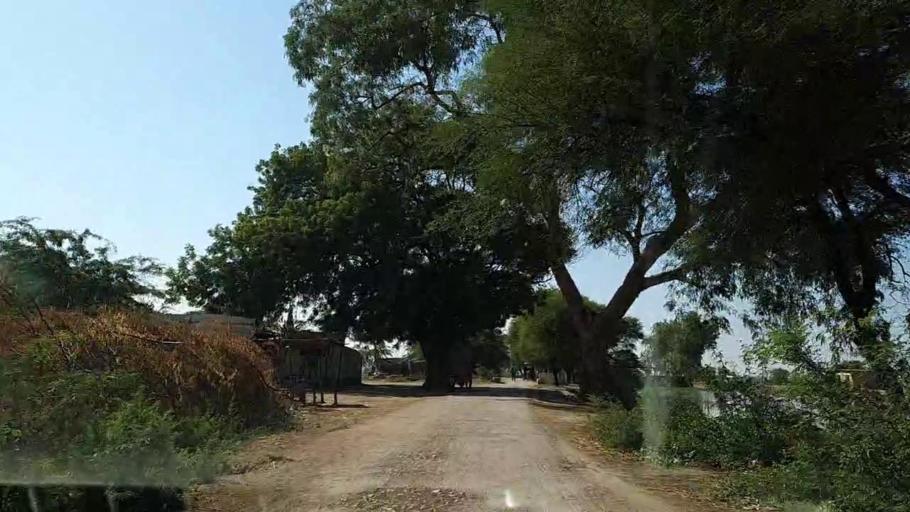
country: PK
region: Sindh
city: Chuhar Jamali
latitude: 24.5697
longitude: 68.0429
